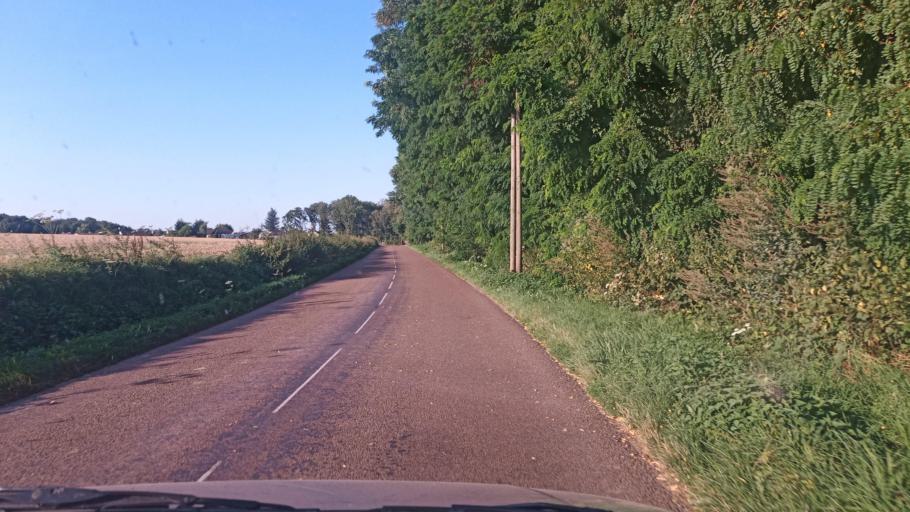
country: FR
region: Bourgogne
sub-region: Departement de l'Yonne
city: Saint-Valerien
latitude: 48.1869
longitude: 3.1055
